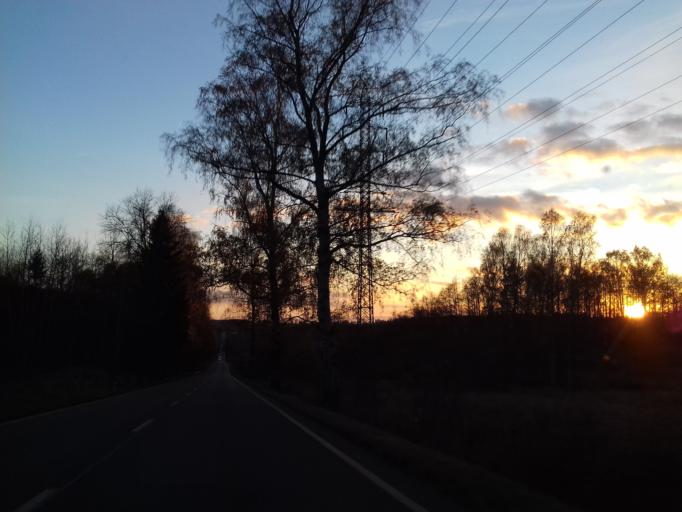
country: CZ
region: Pardubicky
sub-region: Okres Chrudim
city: Hlinsko
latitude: 49.7335
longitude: 15.8743
